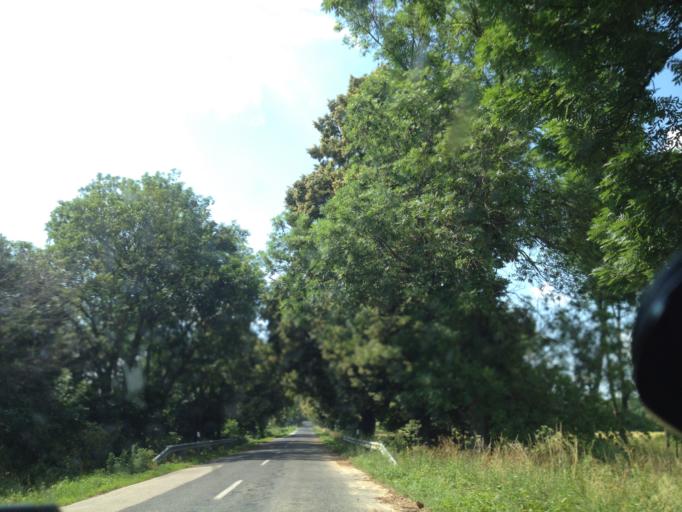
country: HU
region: Veszprem
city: Urkut
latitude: 47.0721
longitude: 17.6872
